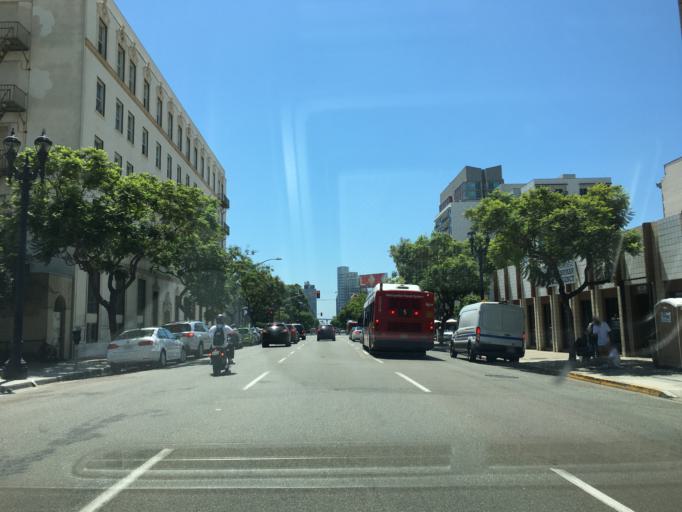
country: US
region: California
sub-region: San Diego County
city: San Diego
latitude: 32.7176
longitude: -117.1557
